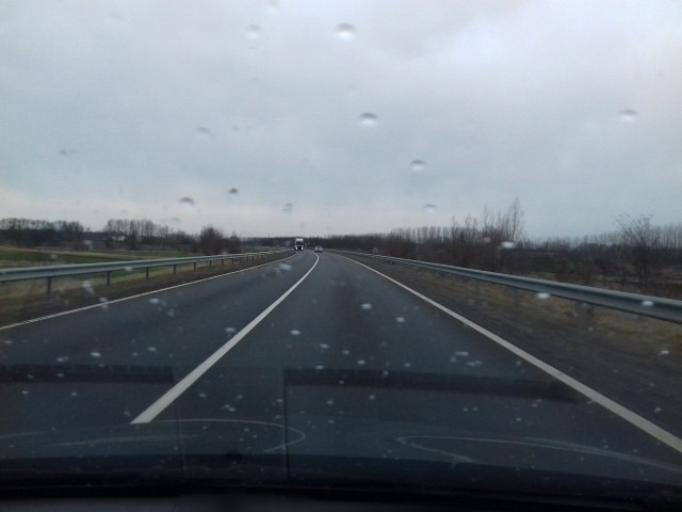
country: HU
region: Szabolcs-Szatmar-Bereg
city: Nyirpazony
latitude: 47.9905
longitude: 21.8224
